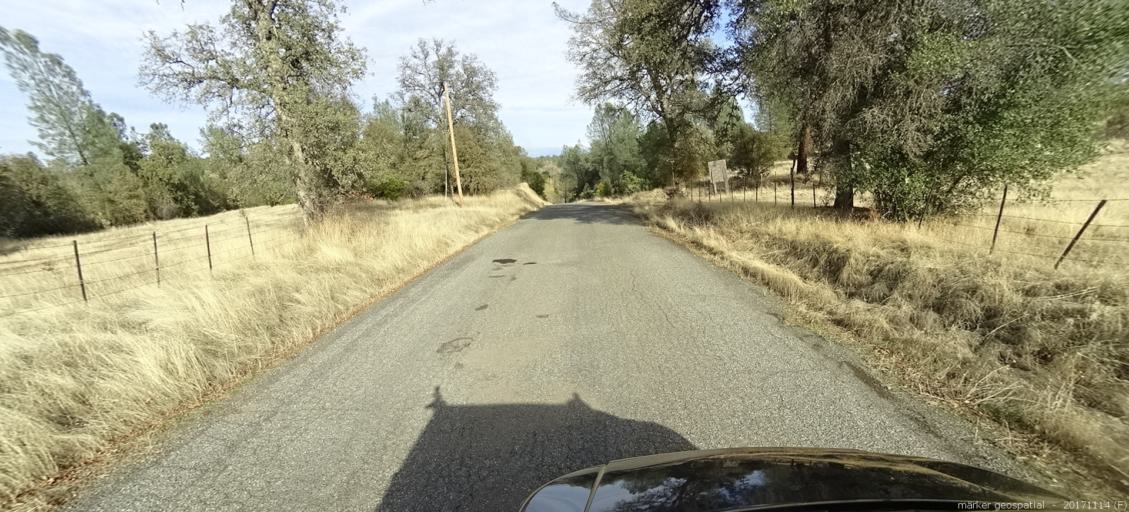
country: US
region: California
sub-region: Shasta County
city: Shasta
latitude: 40.3955
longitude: -122.5314
